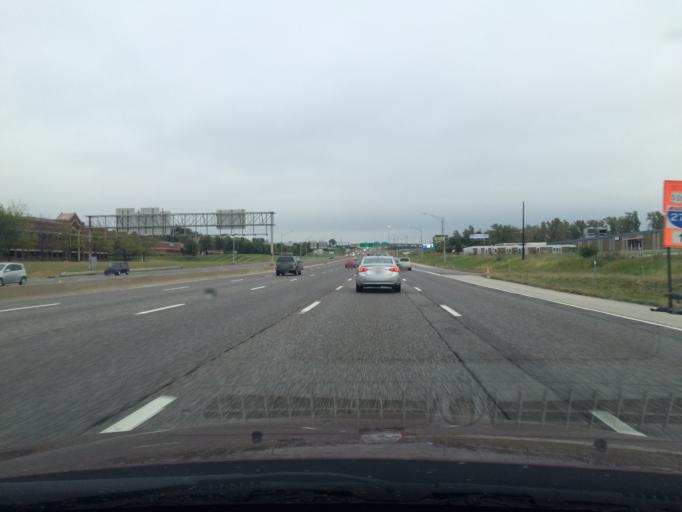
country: US
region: Missouri
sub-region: Saint Charles County
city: Saint Charles
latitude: 38.7543
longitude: -90.4557
